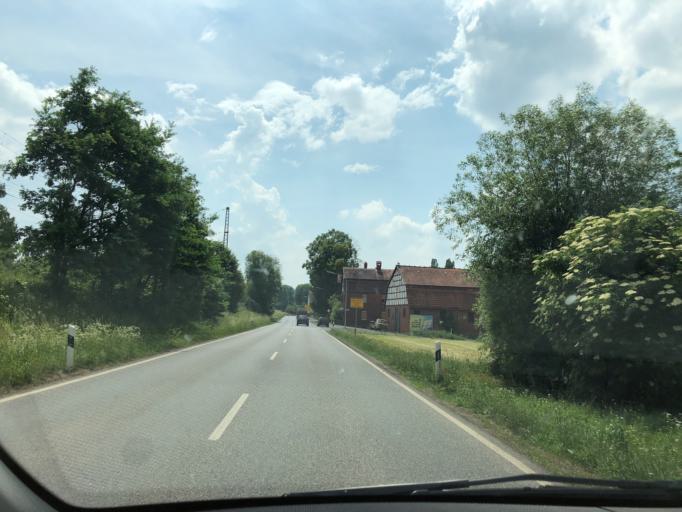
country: DE
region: Hesse
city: Neustadt (Hessen)
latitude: 50.8540
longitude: 9.1223
